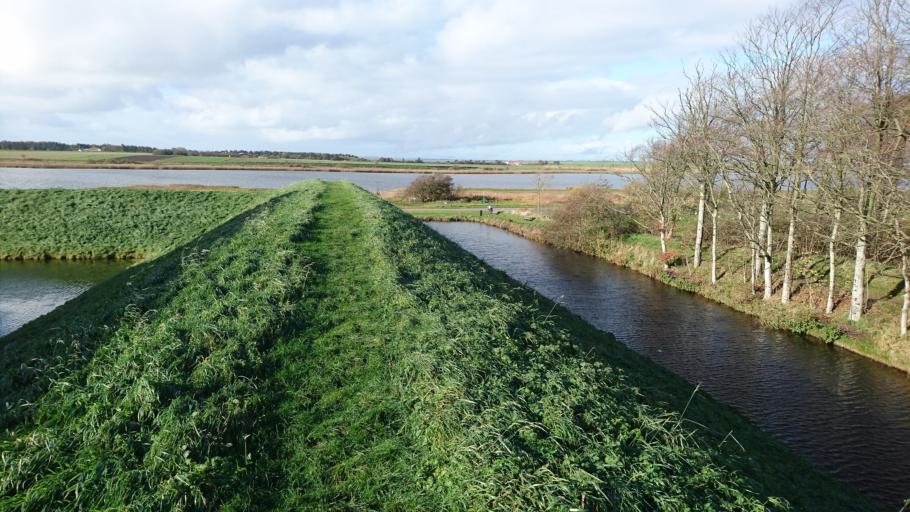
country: DK
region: Central Jutland
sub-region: Holstebro Kommune
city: Vinderup
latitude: 56.6400
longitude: 8.7830
